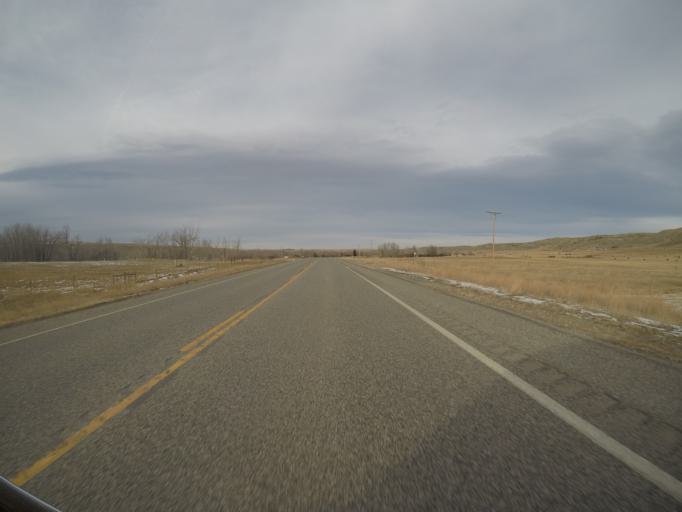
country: US
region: Montana
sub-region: Stillwater County
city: Absarokee
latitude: 45.4490
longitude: -109.4478
